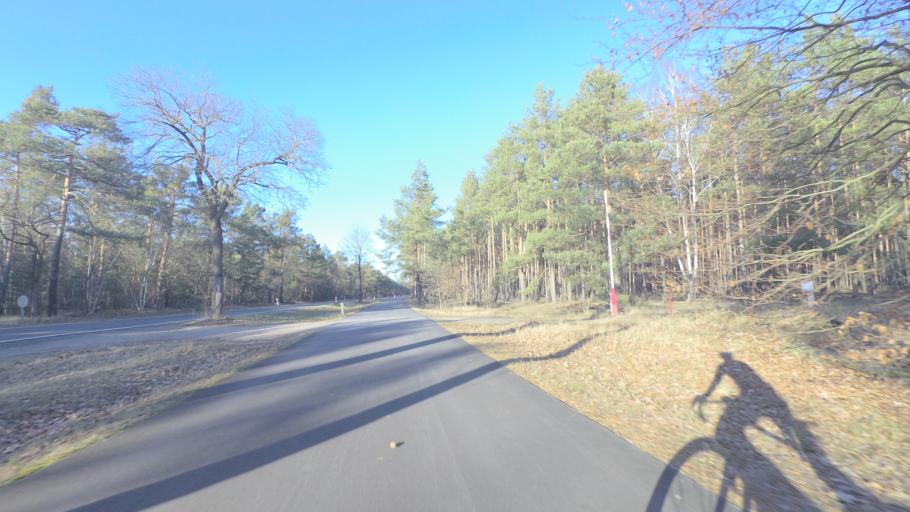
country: DE
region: Brandenburg
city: Sperenberg
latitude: 52.0283
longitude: 13.3185
